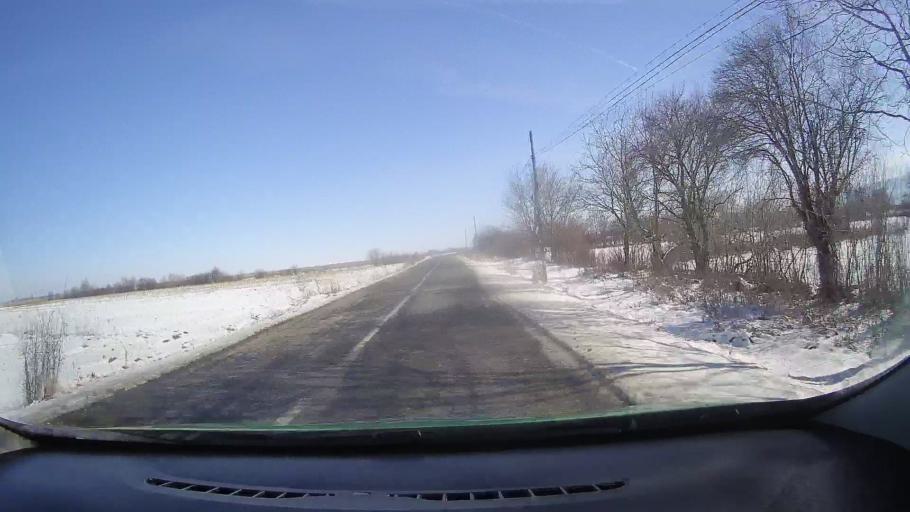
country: RO
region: Brasov
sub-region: Comuna Recea
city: Recea
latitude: 45.7320
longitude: 24.9148
